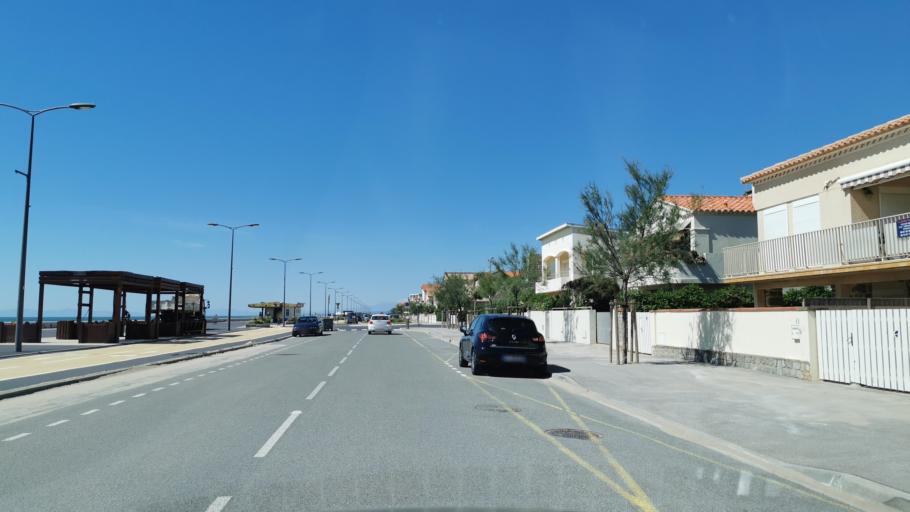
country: FR
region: Languedoc-Roussillon
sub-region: Departement de l'Aude
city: Armissan
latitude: 43.1579
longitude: 3.1668
